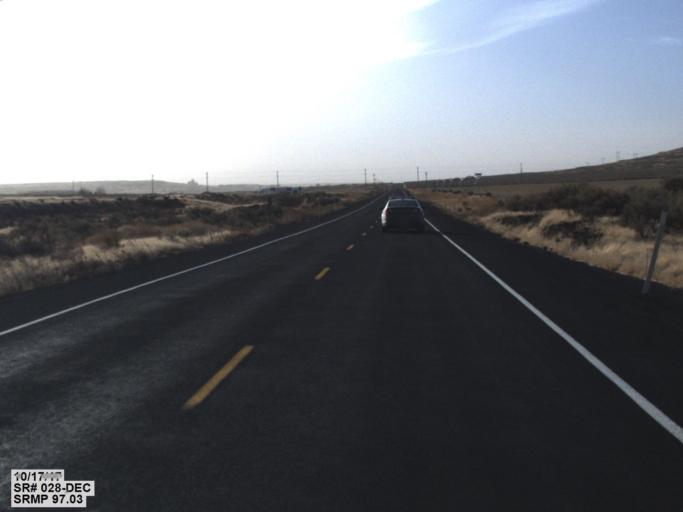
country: US
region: Washington
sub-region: Adams County
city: Ritzville
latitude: 47.3391
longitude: -118.6271
